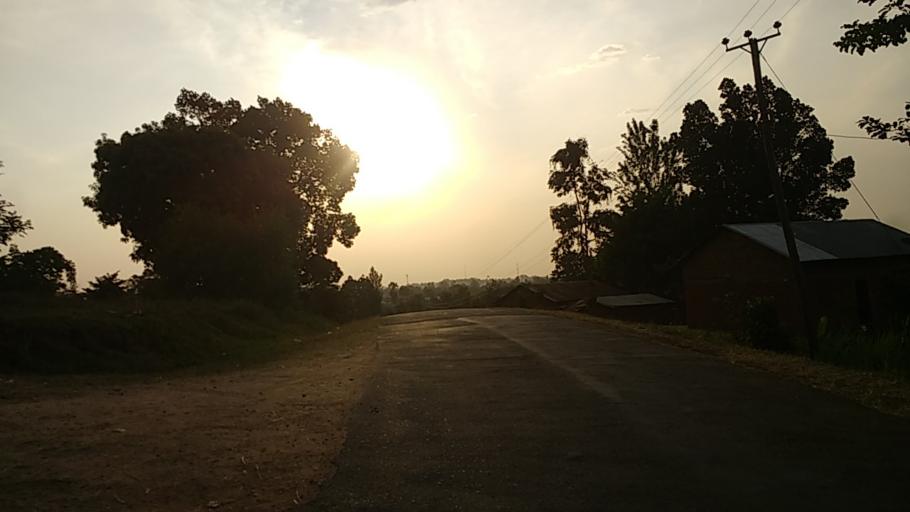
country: UG
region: Eastern Region
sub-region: Mbale District
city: Mbale
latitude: 1.0773
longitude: 34.2104
